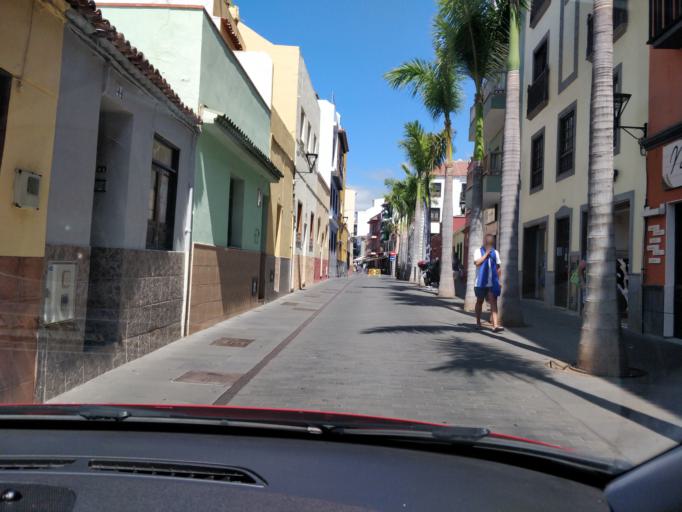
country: ES
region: Canary Islands
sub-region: Provincia de Santa Cruz de Tenerife
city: Puerto de la Cruz
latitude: 28.4175
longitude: -16.5535
